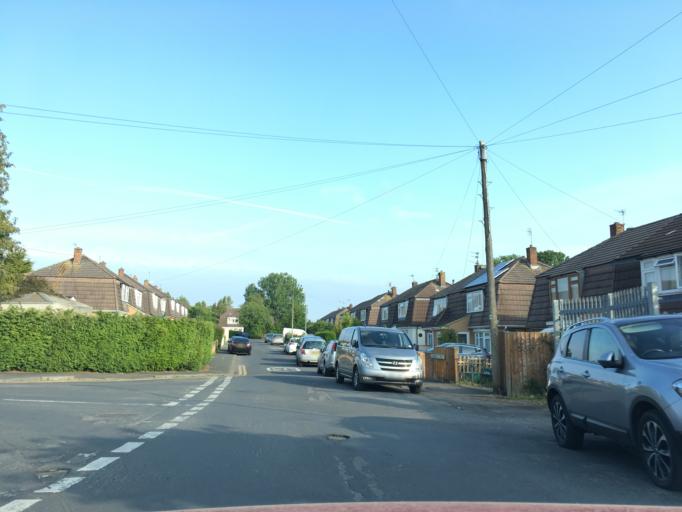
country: GB
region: England
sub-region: South Gloucestershire
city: Stoke Gifford
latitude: 51.5145
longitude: -2.5647
